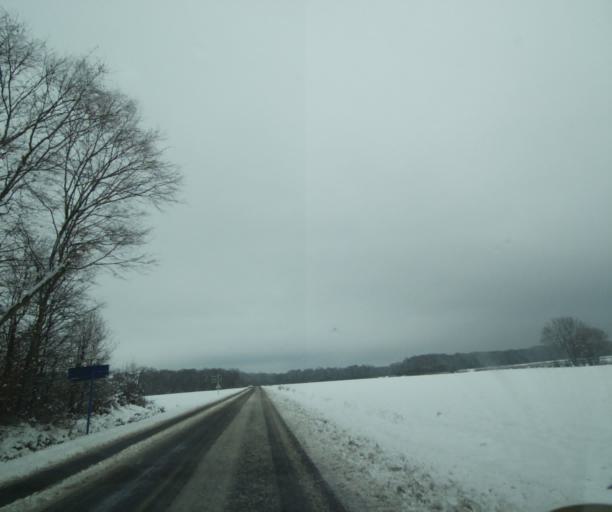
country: FR
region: Champagne-Ardenne
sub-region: Departement de la Haute-Marne
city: Montier-en-Der
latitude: 48.5094
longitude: 4.7479
